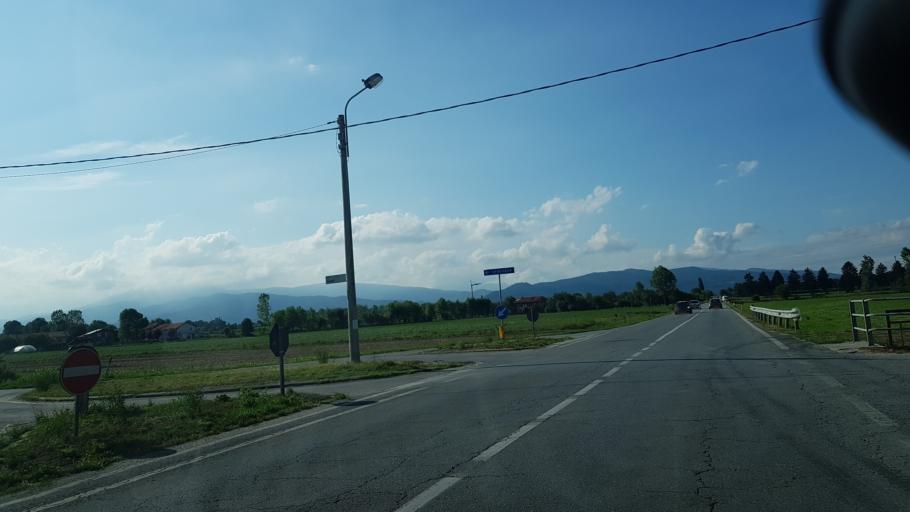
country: IT
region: Piedmont
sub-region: Provincia di Cuneo
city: Roata Rossi
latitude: 44.4579
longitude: 7.5204
